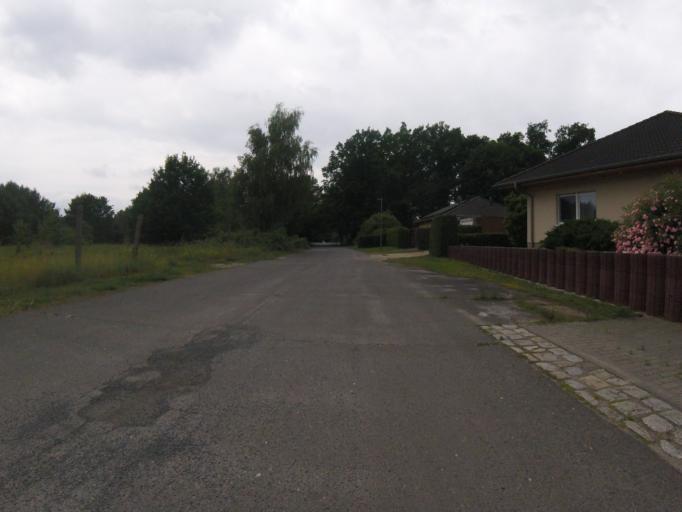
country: DE
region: Brandenburg
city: Bestensee
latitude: 52.2333
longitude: 13.6693
